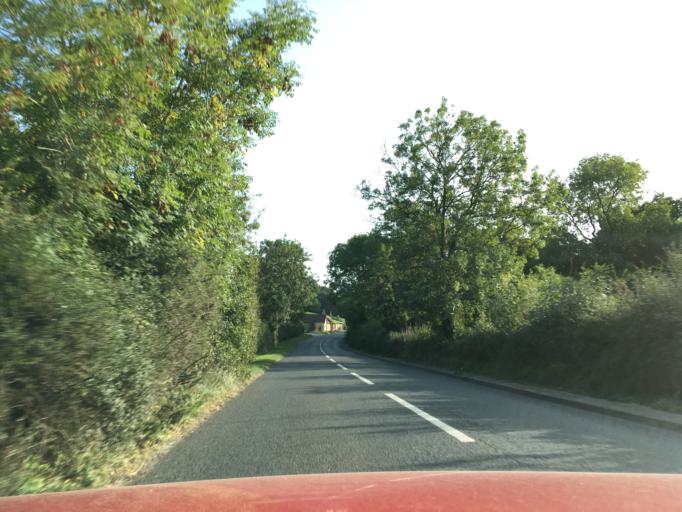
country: GB
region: England
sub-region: Gloucestershire
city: Gloucester
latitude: 51.9182
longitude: -2.2932
